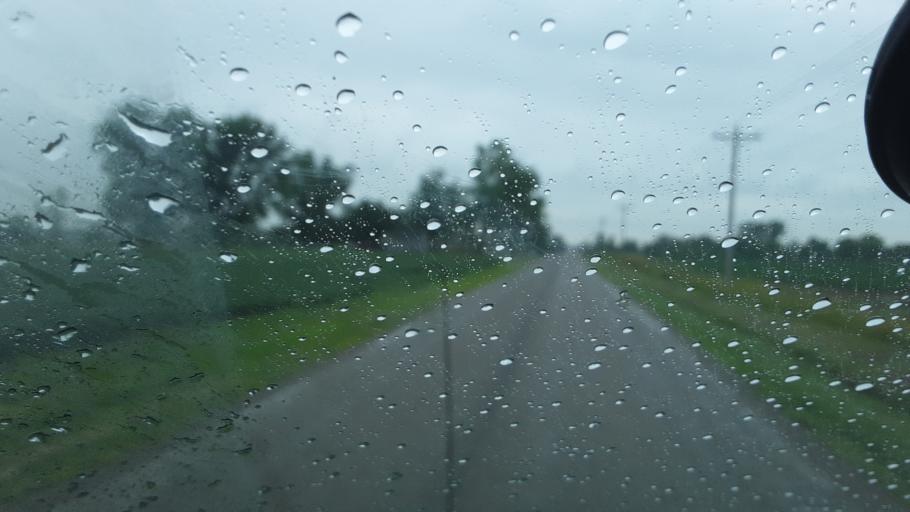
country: US
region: Ohio
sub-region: Williams County
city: Montpelier
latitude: 41.5978
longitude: -84.5743
